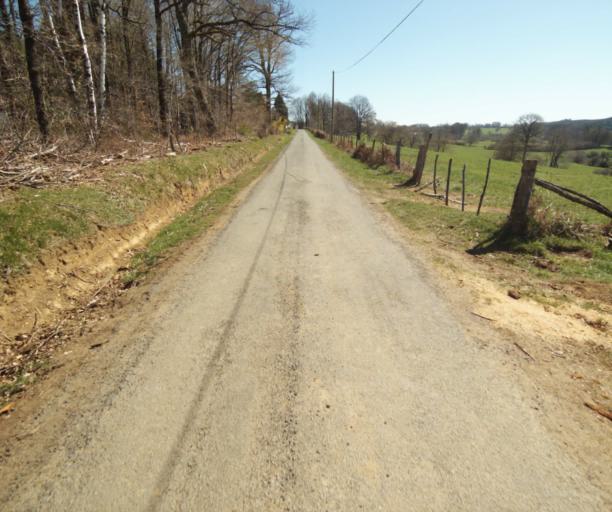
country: FR
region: Limousin
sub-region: Departement de la Correze
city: Uzerche
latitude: 45.4049
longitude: 1.6210
